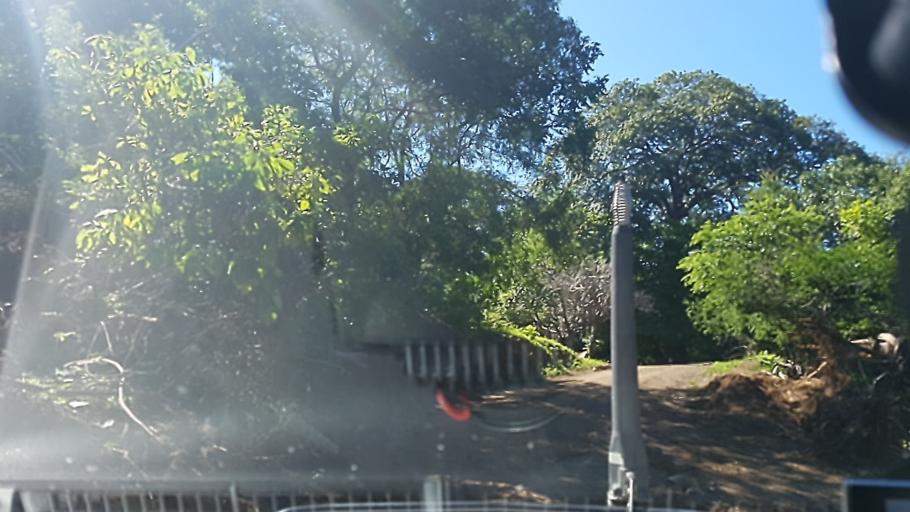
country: NI
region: Rivas
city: Tola
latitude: 11.5422
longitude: -86.0989
